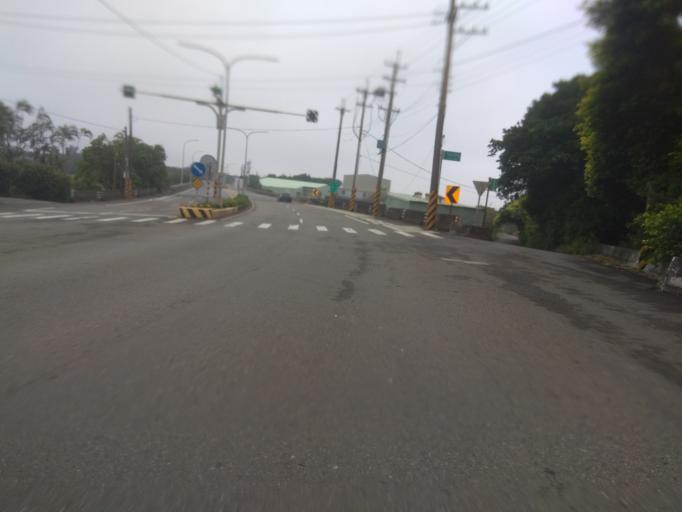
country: TW
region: Taiwan
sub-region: Hsinchu
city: Zhubei
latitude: 24.9981
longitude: 121.0351
